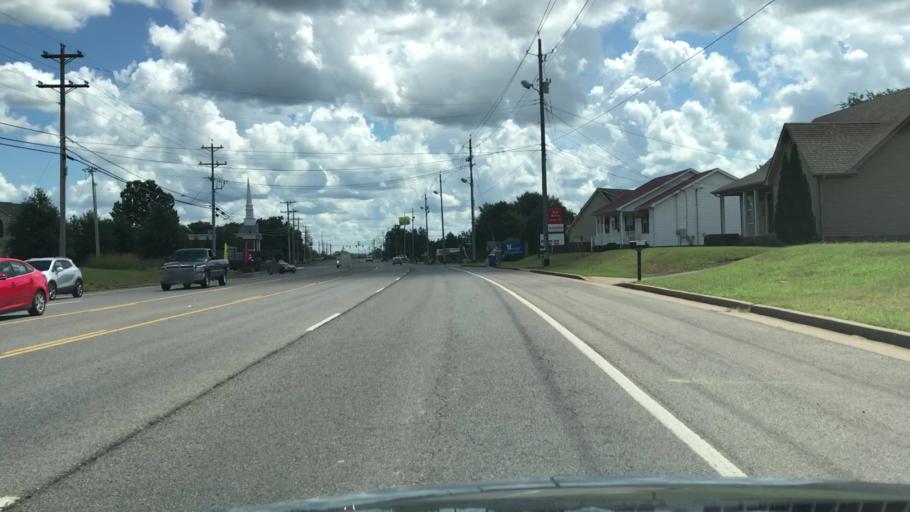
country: US
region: Tennessee
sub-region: Rutherford County
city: Murfreesboro
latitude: 35.8446
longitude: -86.4559
